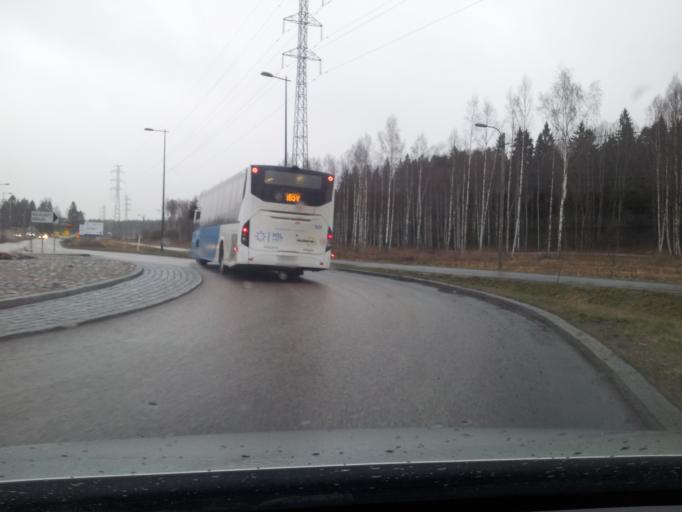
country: FI
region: Uusimaa
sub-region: Helsinki
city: Espoo
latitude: 60.1689
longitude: 24.6207
